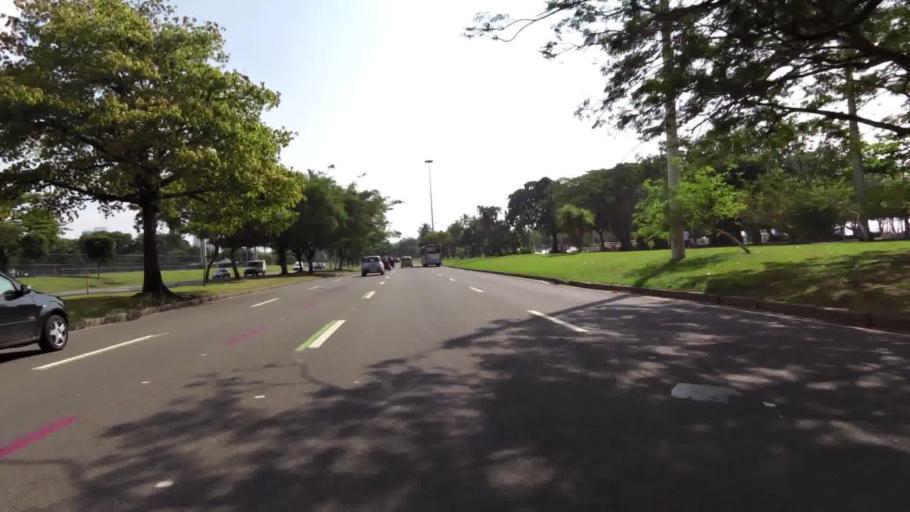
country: BR
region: Rio de Janeiro
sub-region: Rio De Janeiro
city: Rio de Janeiro
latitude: -22.9261
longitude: -43.1715
